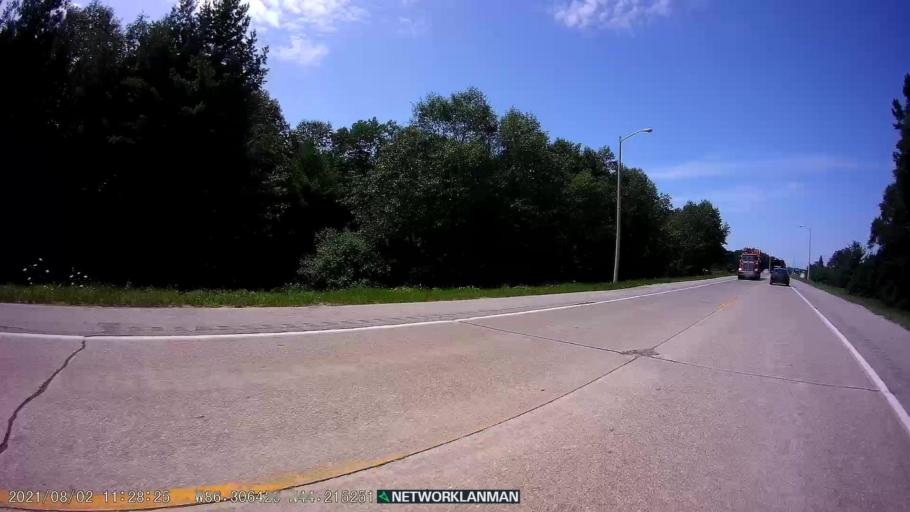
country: US
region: Michigan
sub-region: Manistee County
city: Manistee
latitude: 44.2153
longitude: -86.3061
